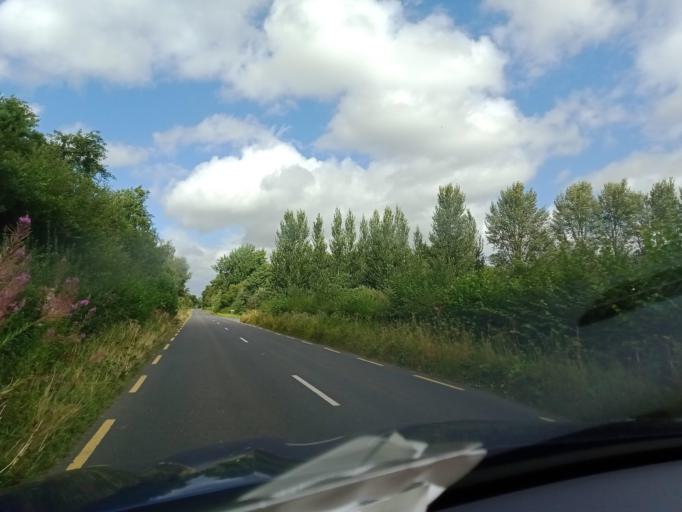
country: IE
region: Leinster
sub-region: Laois
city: Portlaoise
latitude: 52.9842
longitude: -7.2872
